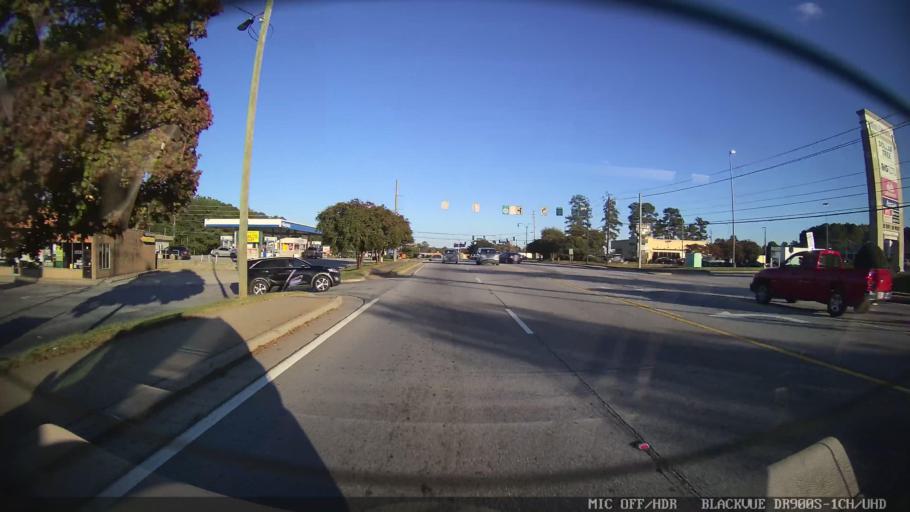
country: US
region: Georgia
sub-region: Henry County
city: Stockbridge
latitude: 33.5535
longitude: -84.2604
